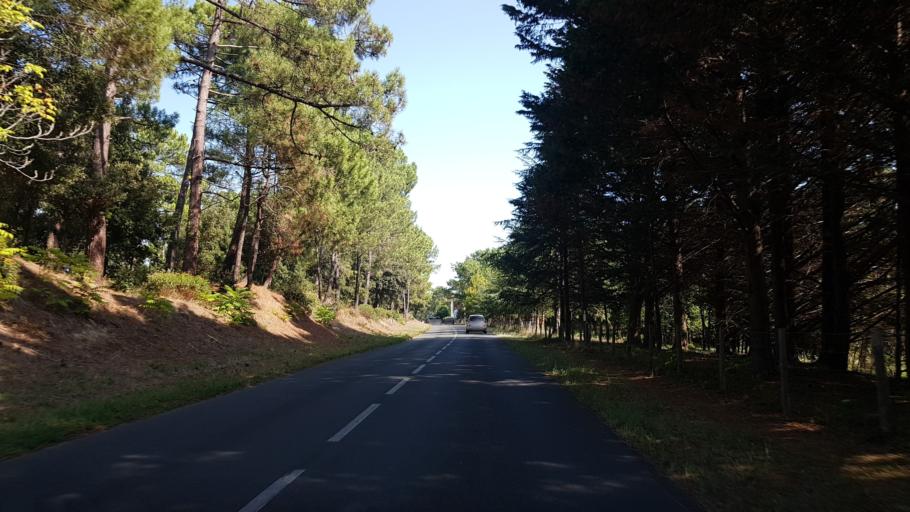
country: FR
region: Poitou-Charentes
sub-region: Departement de la Charente-Maritime
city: Les Mathes
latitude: 45.6991
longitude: -1.2049
